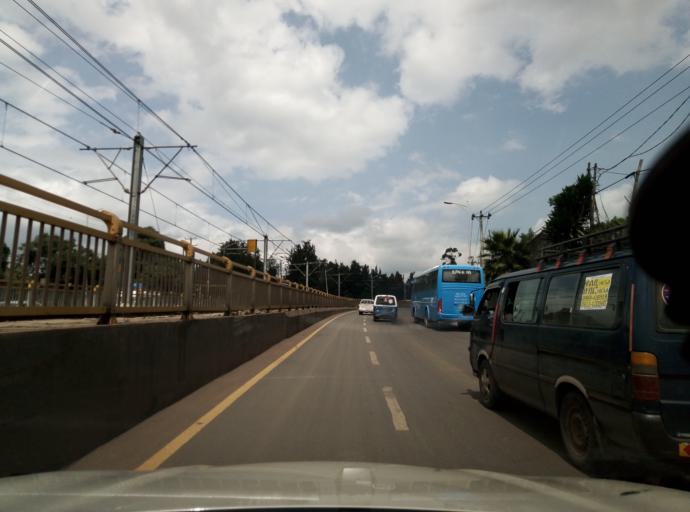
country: ET
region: Adis Abeba
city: Addis Ababa
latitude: 9.0113
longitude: 38.7263
